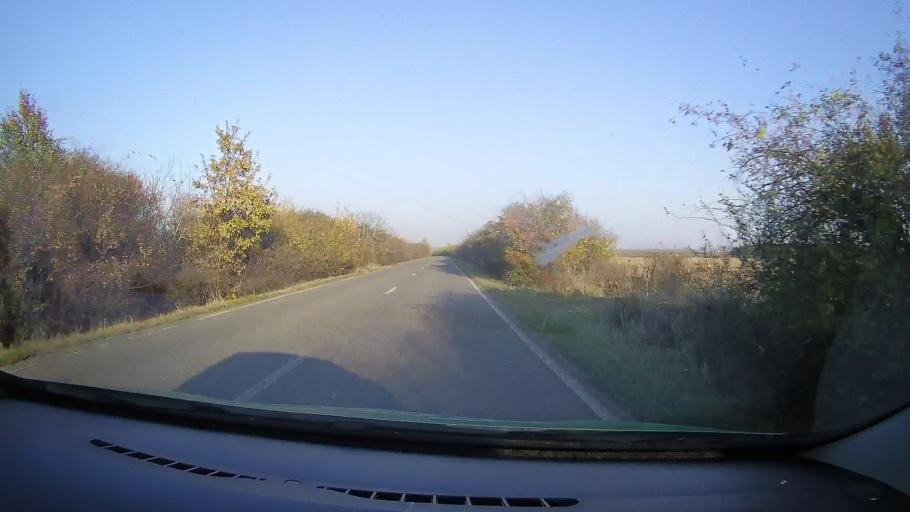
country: RO
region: Arad
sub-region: Comuna Tarnova
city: Chier
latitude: 46.3311
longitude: 21.8568
